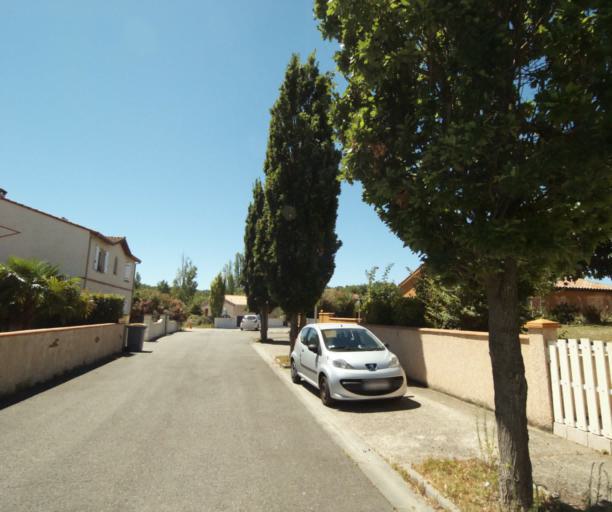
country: FR
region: Midi-Pyrenees
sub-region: Departement de la Haute-Garonne
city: Pechabou
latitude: 43.5122
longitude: 1.5133
